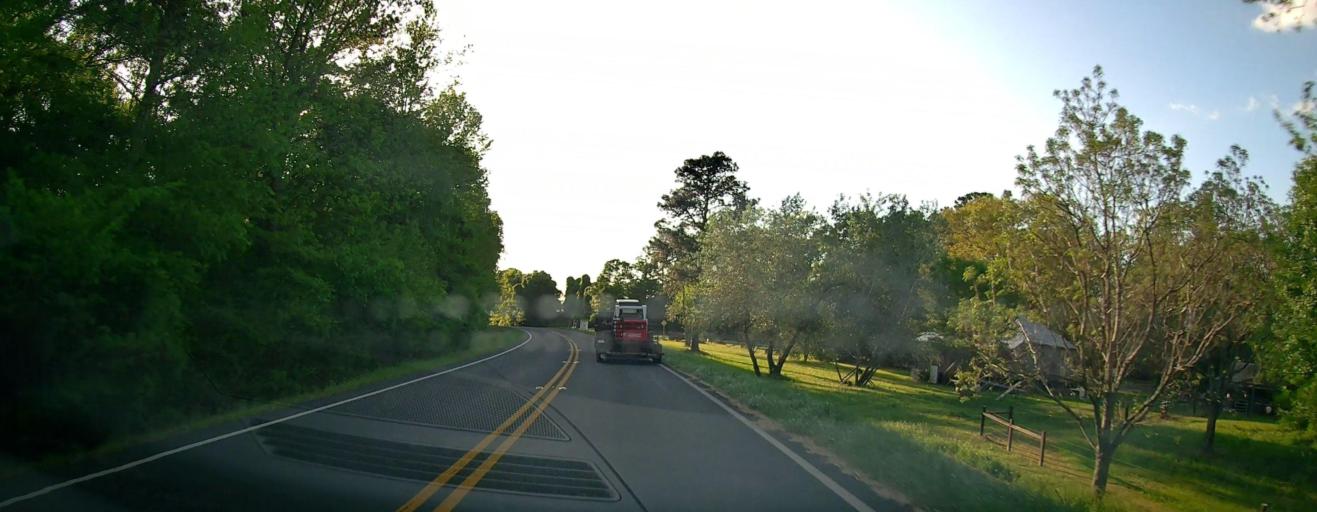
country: US
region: Georgia
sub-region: Walton County
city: Social Circle
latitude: 33.5042
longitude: -83.6542
